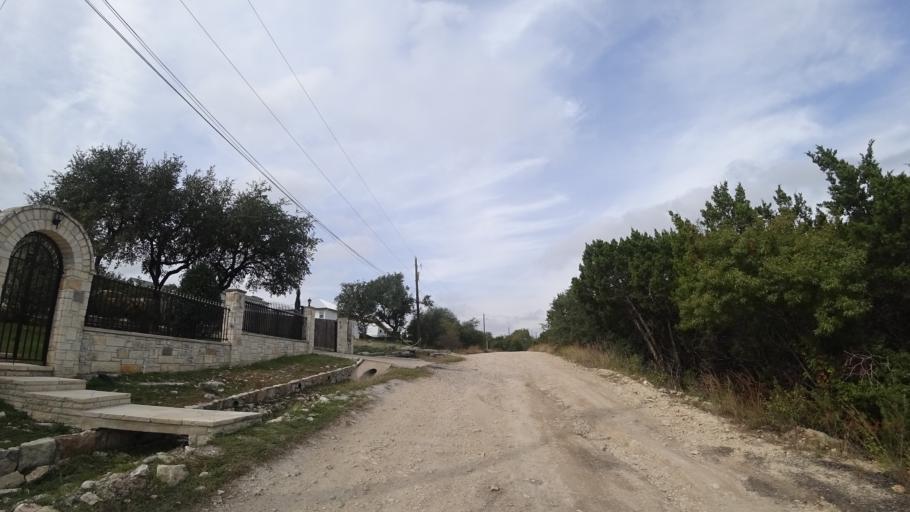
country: US
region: Texas
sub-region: Travis County
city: Hudson Bend
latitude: 30.3913
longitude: -97.9307
